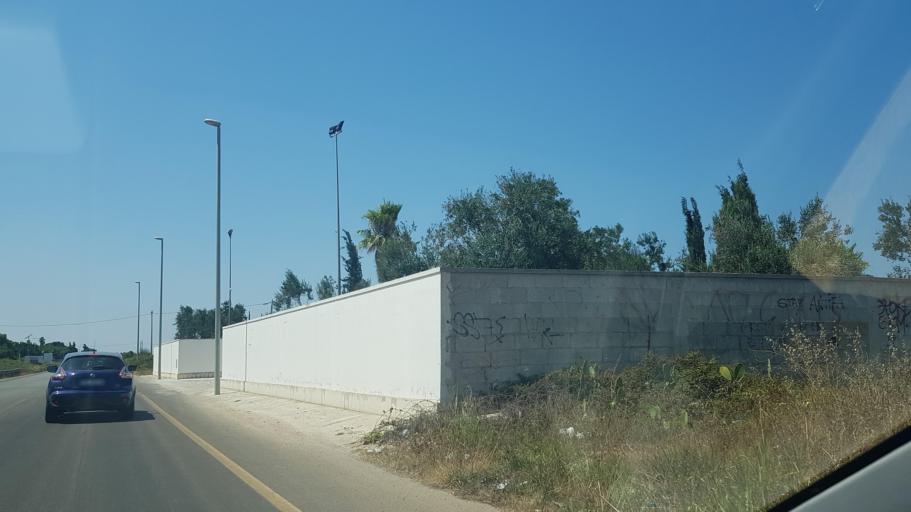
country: IT
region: Apulia
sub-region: Provincia di Lecce
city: Merine
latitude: 40.3361
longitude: 18.2335
